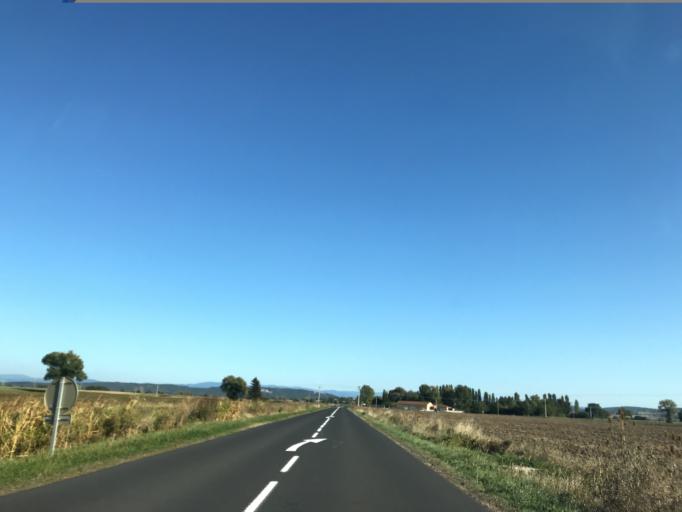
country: FR
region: Auvergne
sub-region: Departement du Puy-de-Dome
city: Vertaizon
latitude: 45.7826
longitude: 3.3163
